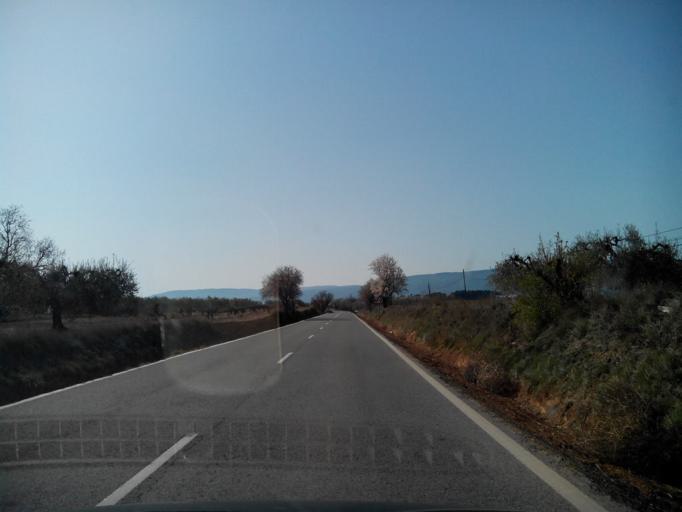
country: ES
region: Catalonia
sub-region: Provincia de Tarragona
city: Blancafort
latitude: 41.4162
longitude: 1.1983
